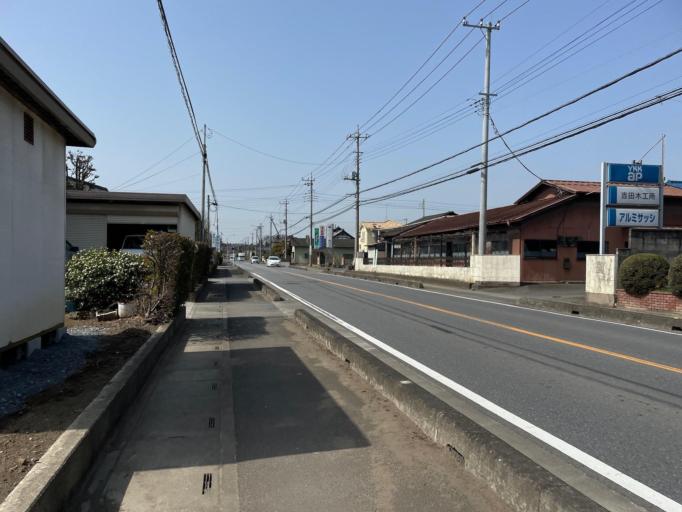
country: JP
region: Saitama
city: Ogawa
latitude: 36.1028
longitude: 139.2686
